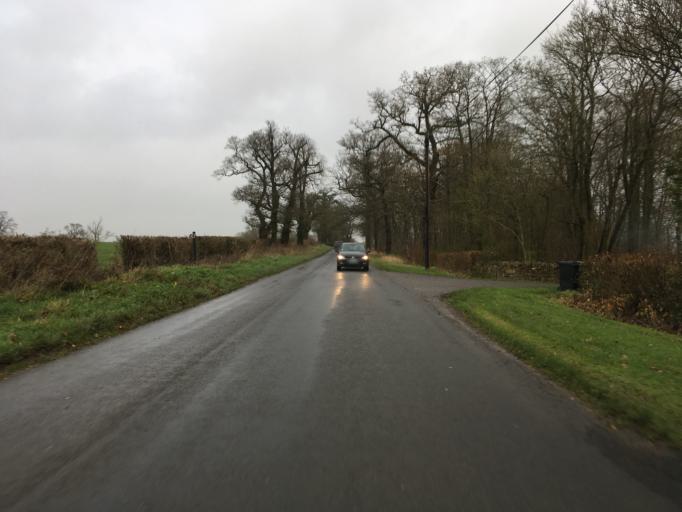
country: GB
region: England
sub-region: Wiltshire
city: Luckington
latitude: 51.5344
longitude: -2.2104
